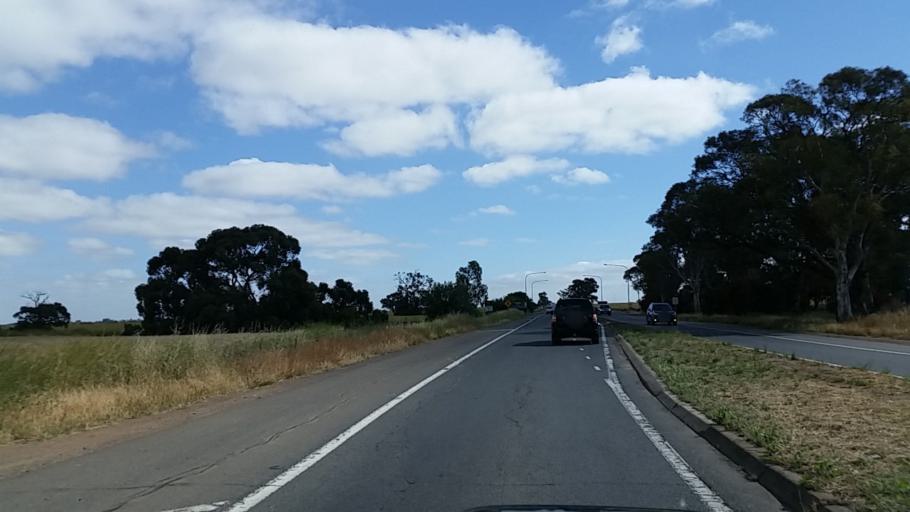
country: AU
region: South Australia
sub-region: Light
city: Willaston
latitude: -34.5683
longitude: 138.7461
